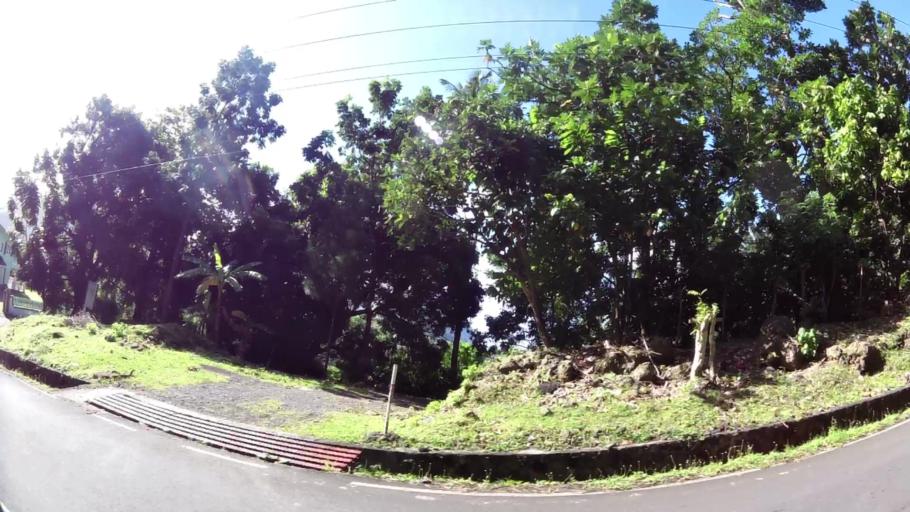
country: LC
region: Soufriere
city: Soufriere
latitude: 13.8643
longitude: -61.0509
